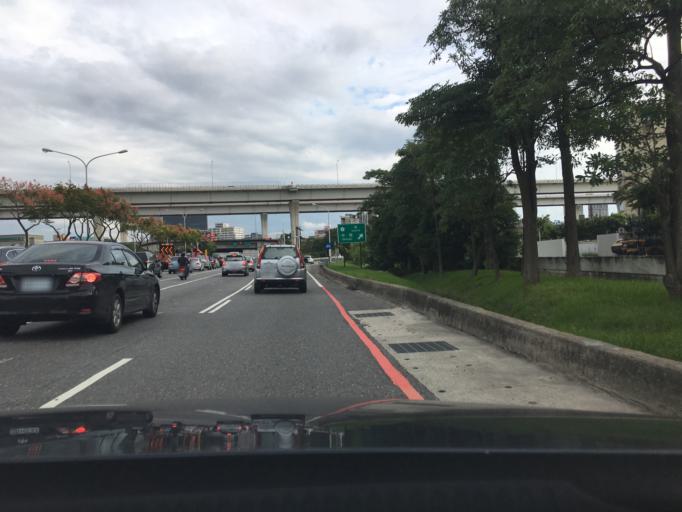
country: TW
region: Taiwan
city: Taoyuan City
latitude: 25.0397
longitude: 121.2962
